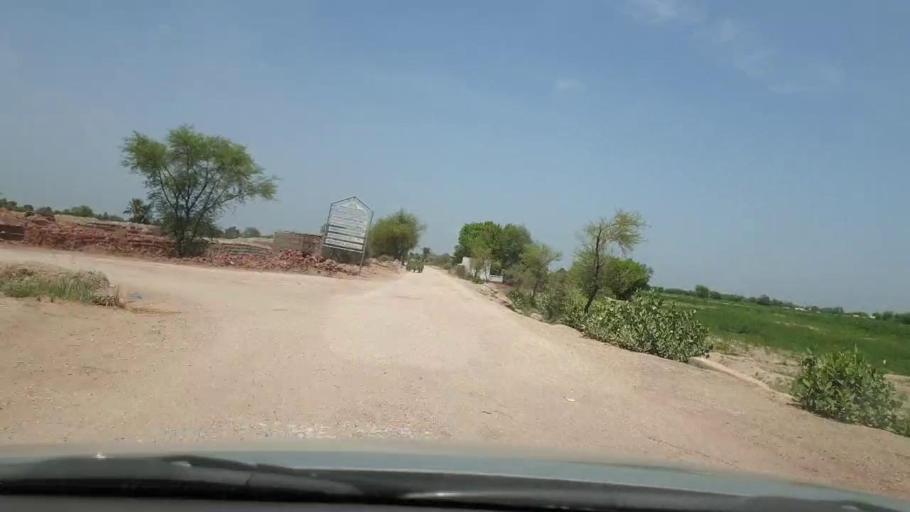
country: PK
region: Sindh
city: Pano Aqil
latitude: 27.7014
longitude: 69.2179
